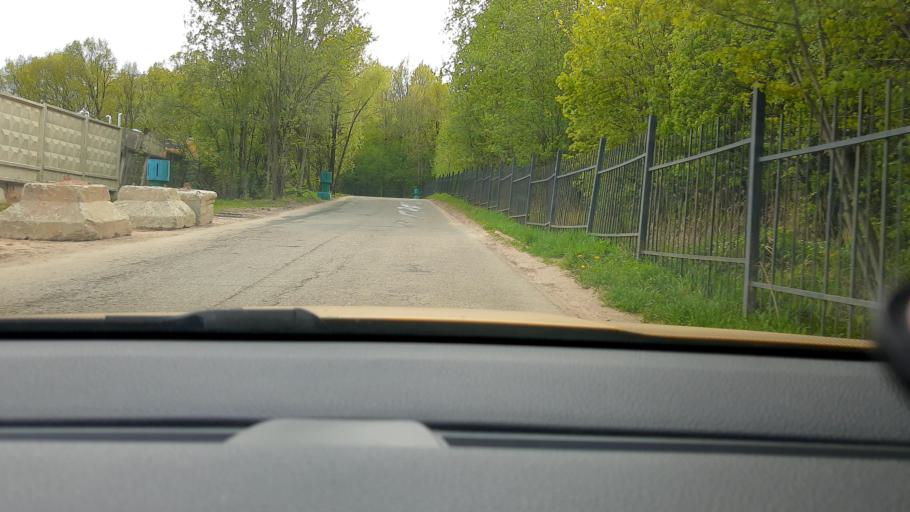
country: RU
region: Moskovskaya
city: Pavshino
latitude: 55.8499
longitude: 37.3761
